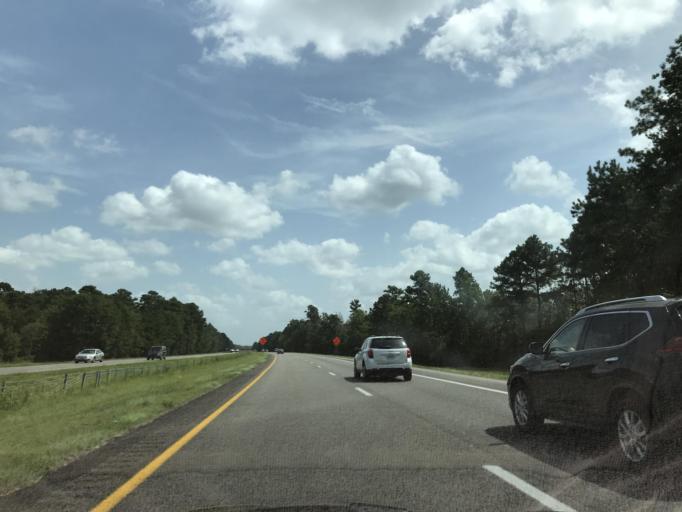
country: US
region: North Carolina
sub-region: Pender County
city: Burgaw
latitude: 34.6240
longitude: -77.9325
